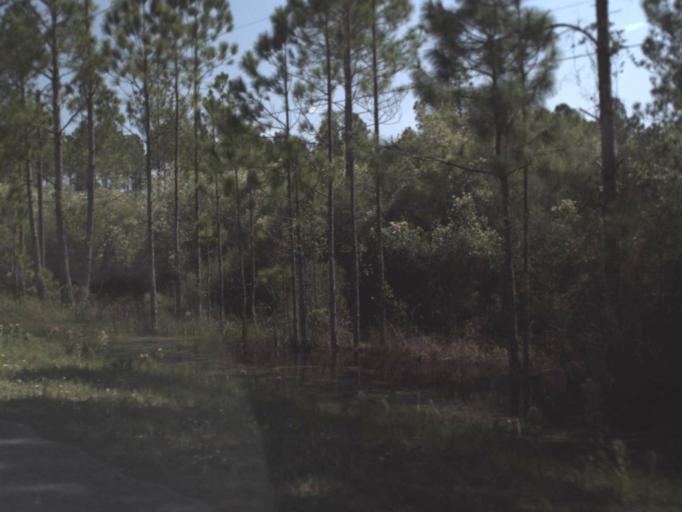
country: US
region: Florida
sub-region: Franklin County
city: Apalachicola
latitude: 29.7278
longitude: -85.1313
